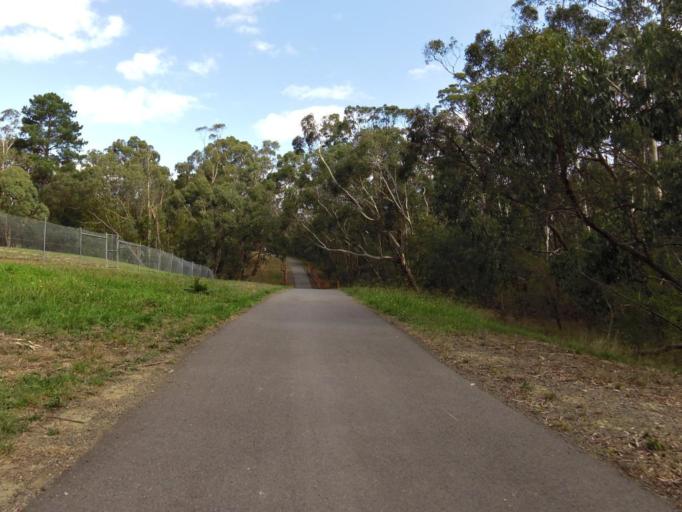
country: AU
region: Victoria
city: Mitcham
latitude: -37.7983
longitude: 145.2037
